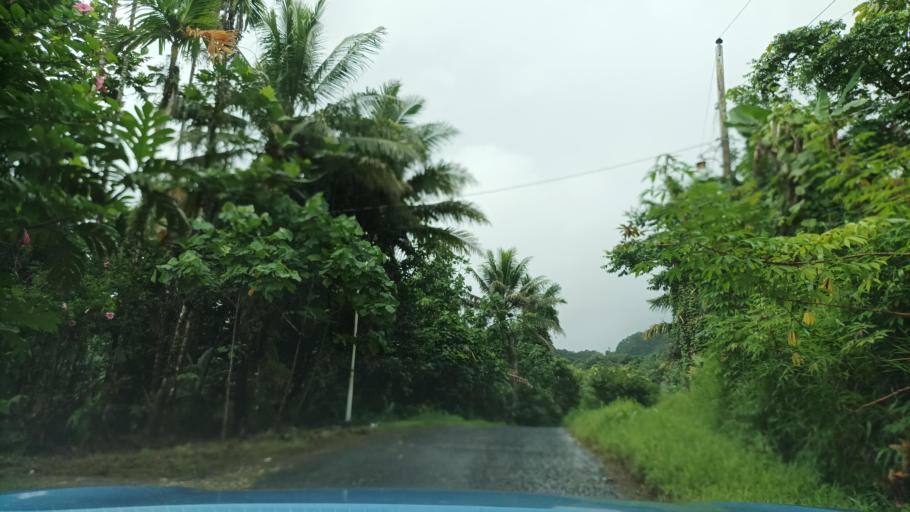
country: FM
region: Pohnpei
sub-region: Kolonia Municipality
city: Kolonia
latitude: 6.9170
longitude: 158.2747
